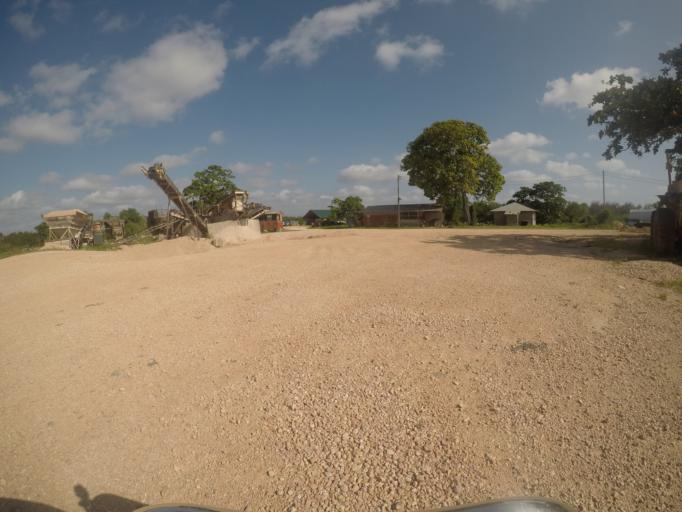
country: TZ
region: Zanzibar Central/South
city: Koani
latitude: -6.2160
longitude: 39.3334
